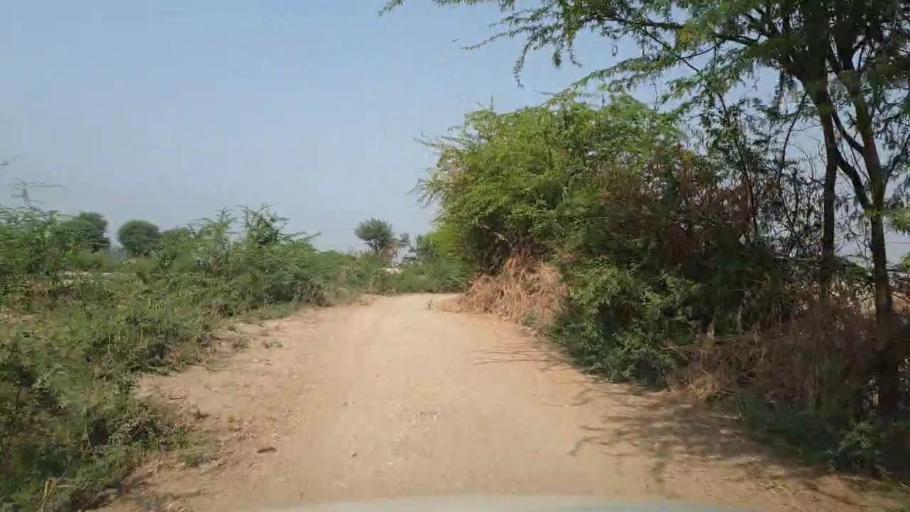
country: PK
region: Sindh
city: Chor
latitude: 25.4632
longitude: 69.7062
